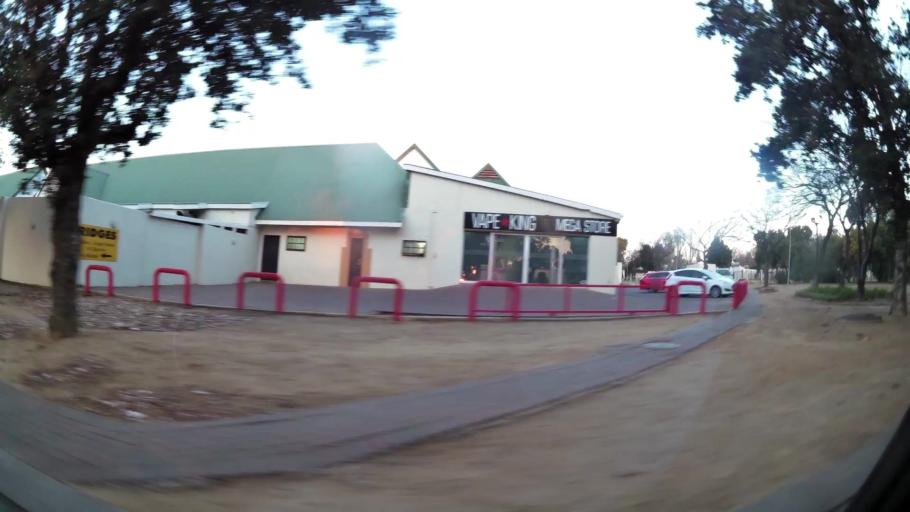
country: ZA
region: Gauteng
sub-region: City of Johannesburg Metropolitan Municipality
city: Diepsloot
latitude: -26.0274
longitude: 28.0206
